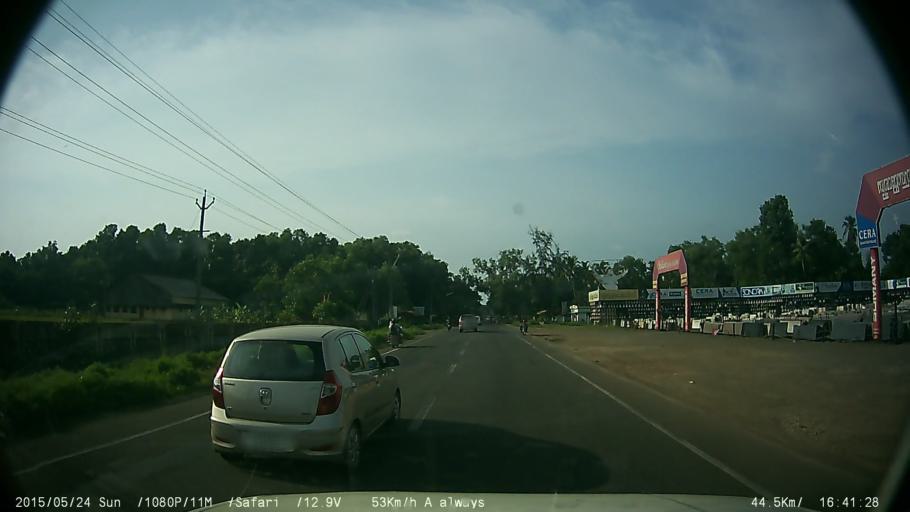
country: IN
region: Kerala
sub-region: Alappuzha
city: Shertallai
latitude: 9.6321
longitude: 76.3337
